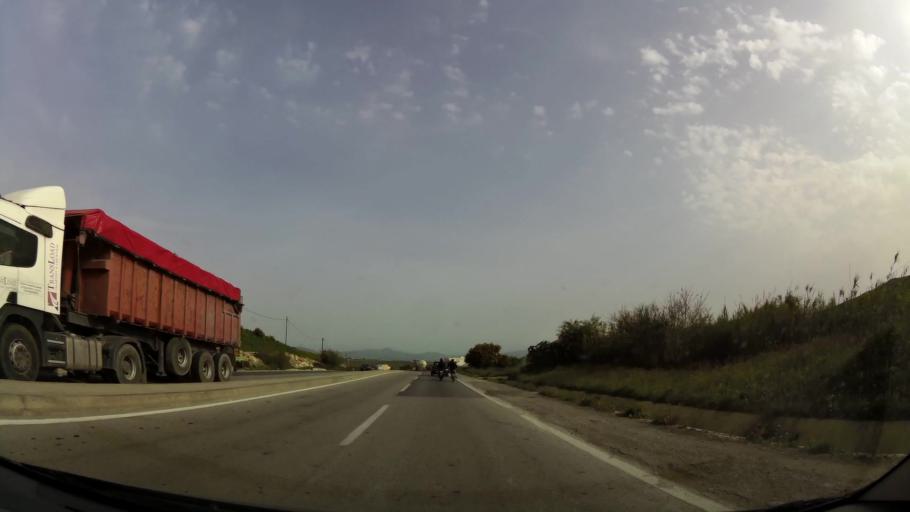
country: MA
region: Tanger-Tetouan
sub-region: Tanger-Assilah
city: Dar Chaoui
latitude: 35.6614
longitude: -5.6970
